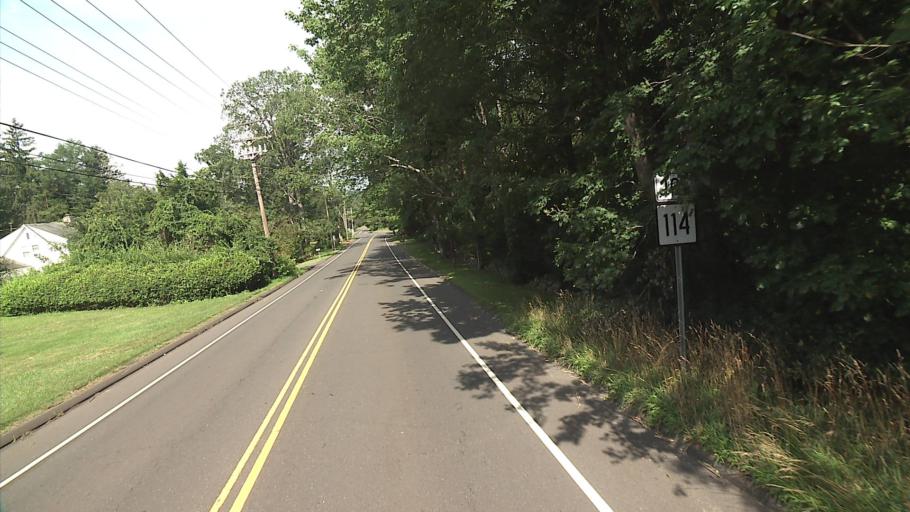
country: US
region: Connecticut
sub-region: New Haven County
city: Woodbridge
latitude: 41.3287
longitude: -73.0229
